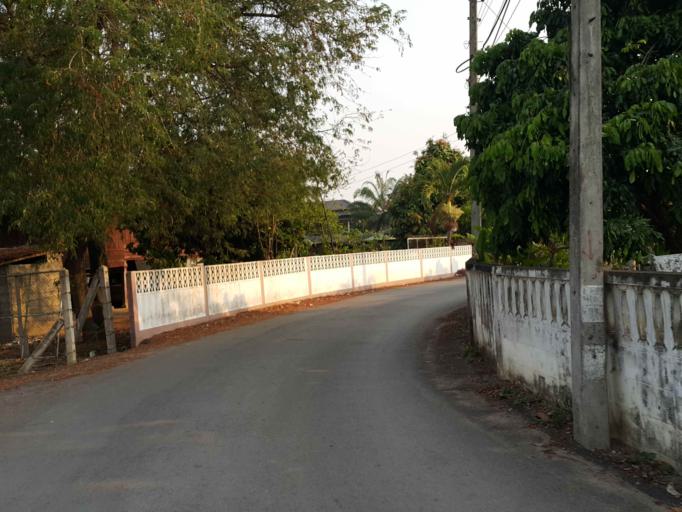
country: TH
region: Chiang Mai
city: Mae Taeng
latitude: 19.0415
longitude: 98.9770
